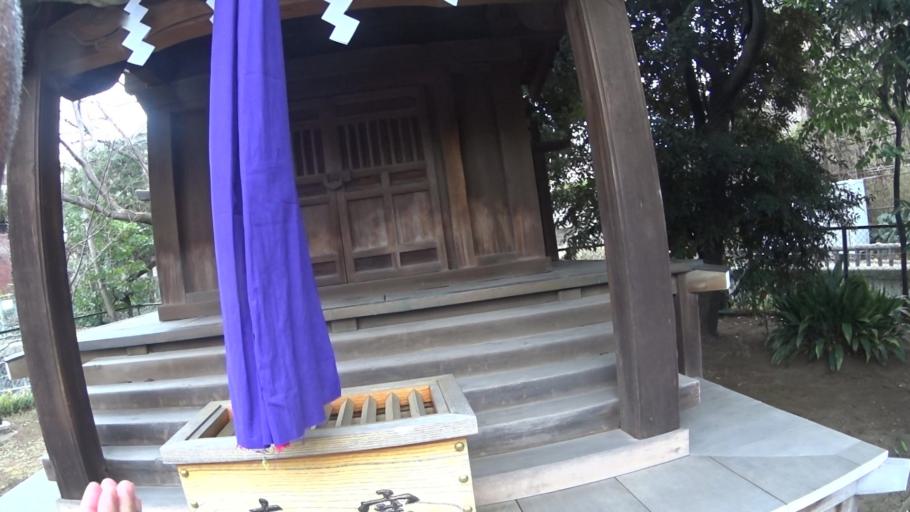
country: JP
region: Kanagawa
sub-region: Kawasaki-shi
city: Kawasaki
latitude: 35.5879
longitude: 139.7210
